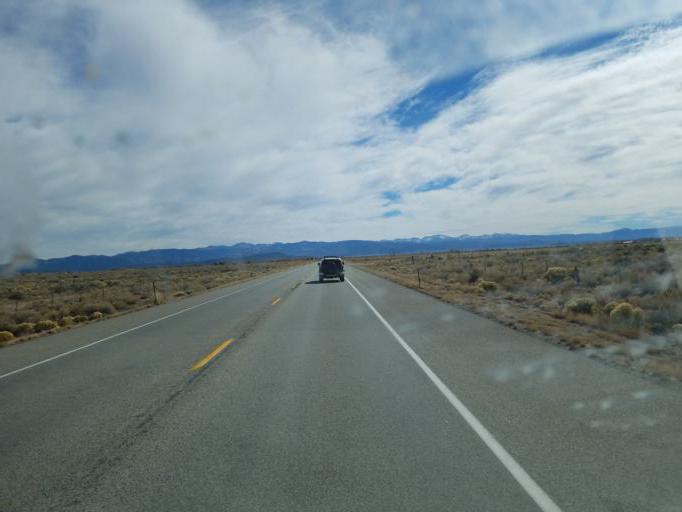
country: US
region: Colorado
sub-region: Costilla County
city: San Luis
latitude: 37.4473
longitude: -105.5381
